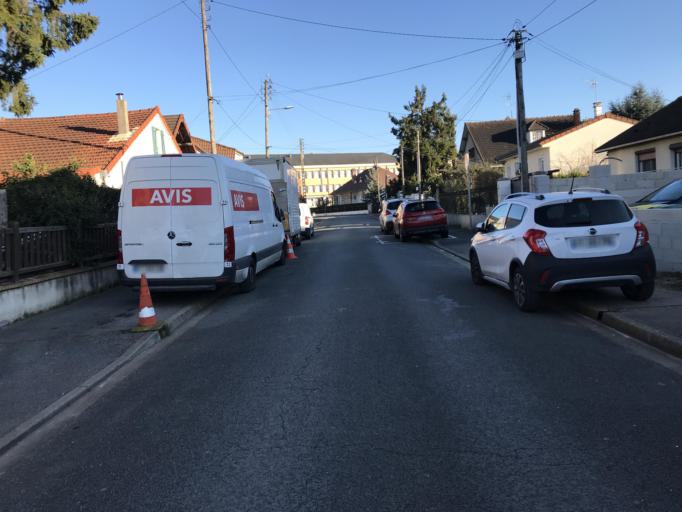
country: FR
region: Ile-de-France
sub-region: Departement de l'Essonne
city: Morangis
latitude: 48.7033
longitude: 2.3325
